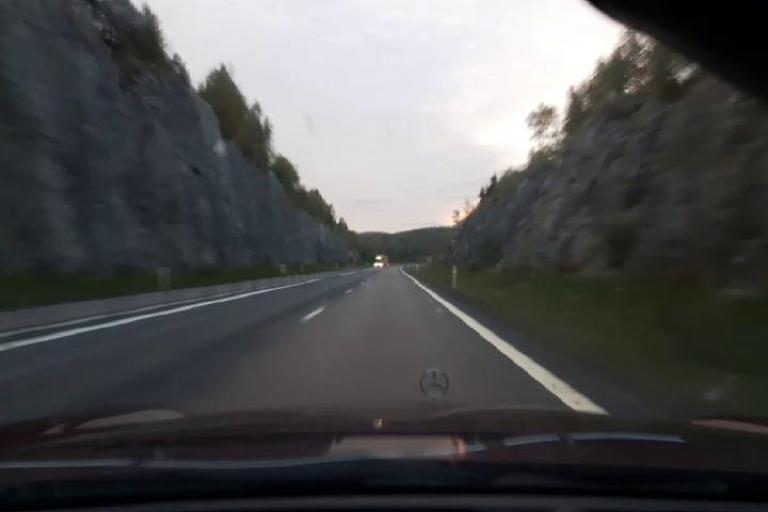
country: SE
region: Vaesternorrland
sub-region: Haernoesands Kommun
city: Haernoesand
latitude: 62.8354
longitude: 17.9682
